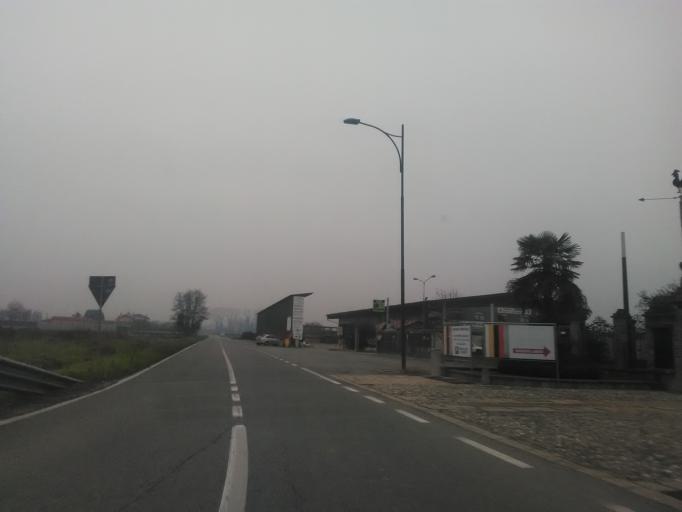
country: IT
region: Piedmont
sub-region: Provincia di Vercelli
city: Cigliano
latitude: 45.3176
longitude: 8.0285
